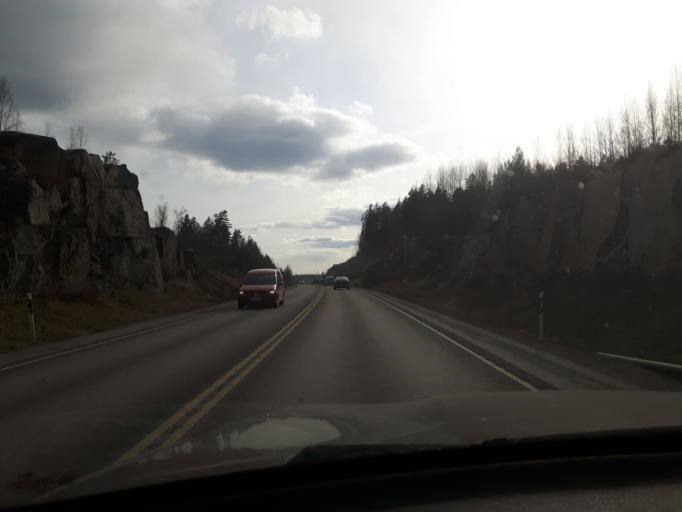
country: FI
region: Pirkanmaa
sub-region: Tampere
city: Kuhmalahti
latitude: 61.7283
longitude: 24.6634
